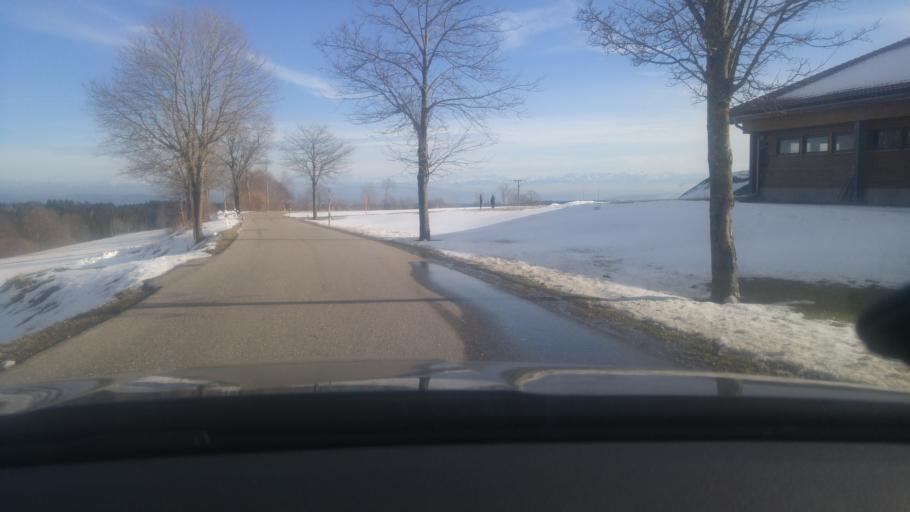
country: DE
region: Baden-Wuerttemberg
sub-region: Freiburg Region
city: Hochenschwand
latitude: 47.7198
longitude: 8.1529
